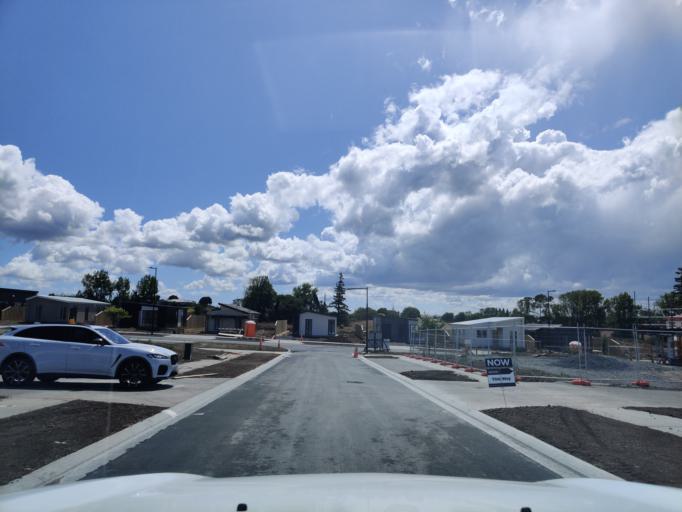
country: NZ
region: Waikato
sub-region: Waikato District
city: Te Kauwhata
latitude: -37.4139
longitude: 175.1500
